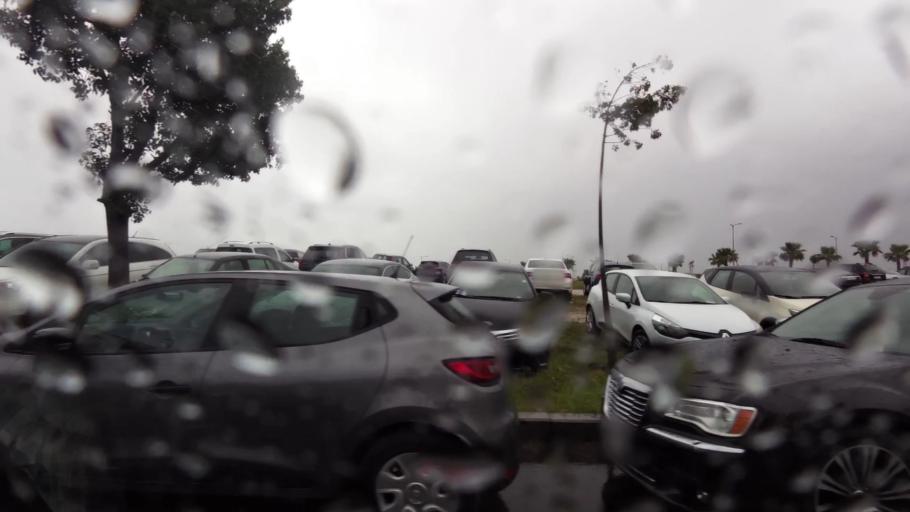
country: MA
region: Grand Casablanca
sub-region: Casablanca
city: Casablanca
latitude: 33.5464
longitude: -7.6697
